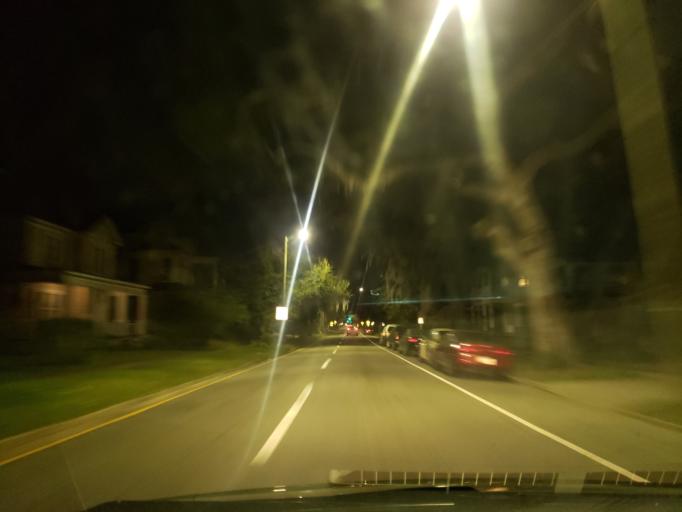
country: US
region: Georgia
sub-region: Chatham County
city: Savannah
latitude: 32.0580
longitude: -81.0782
